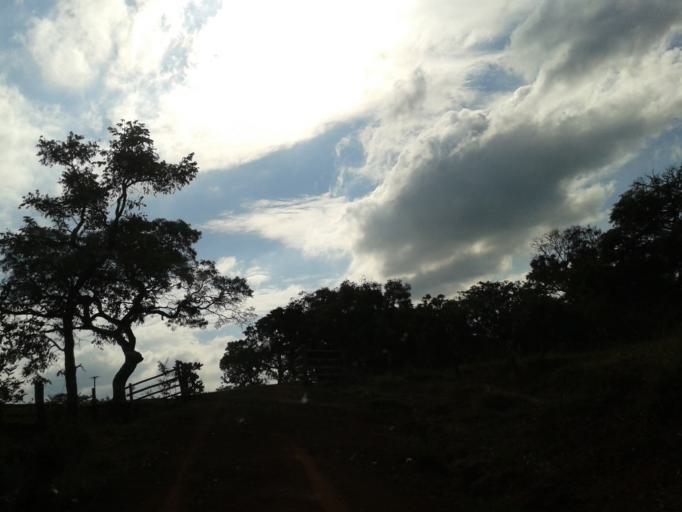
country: BR
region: Minas Gerais
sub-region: Campina Verde
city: Campina Verde
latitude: -19.3905
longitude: -49.6979
